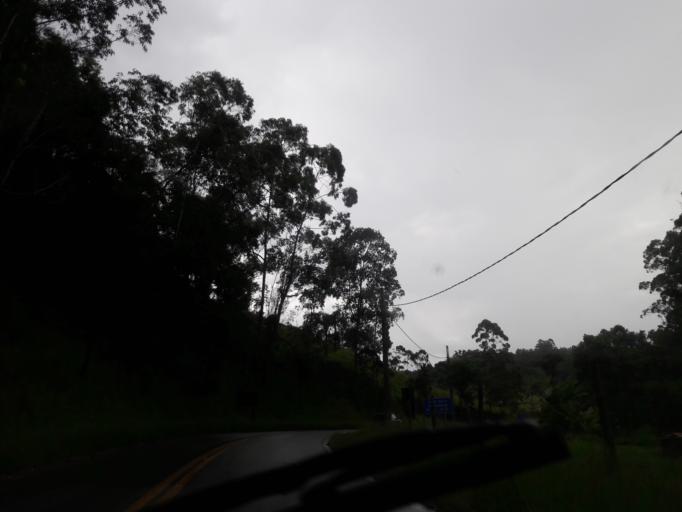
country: BR
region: Sao Paulo
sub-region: Aruja
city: Aruja
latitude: -23.2833
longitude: -46.4244
